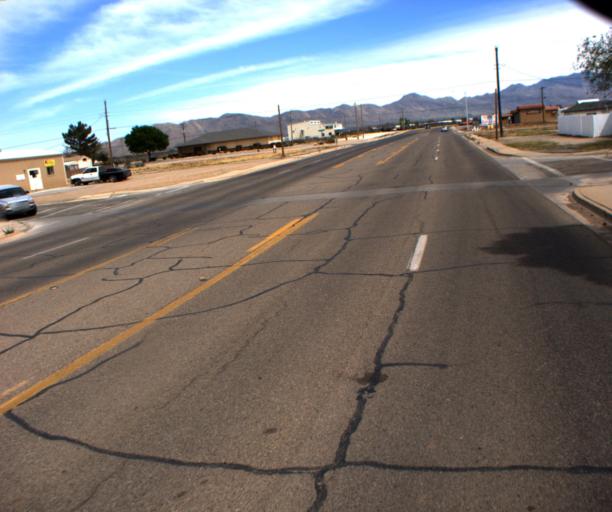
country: US
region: Arizona
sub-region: Cochise County
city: Willcox
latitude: 32.2640
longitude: -109.8352
